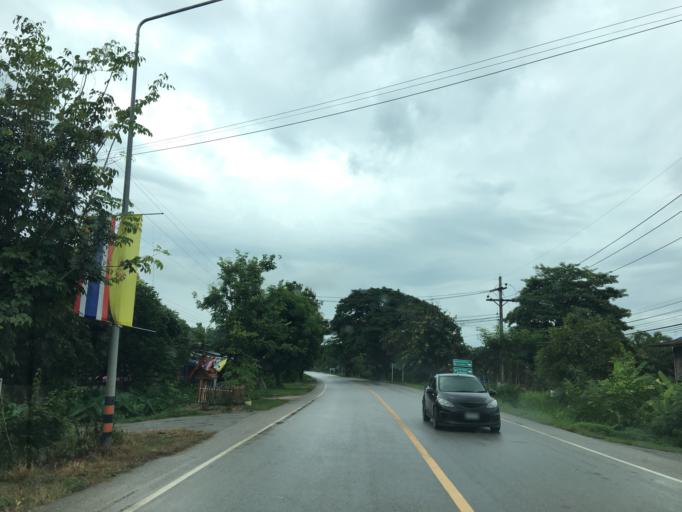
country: TH
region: Chiang Rai
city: Pa Daet
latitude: 19.4976
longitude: 99.9720
